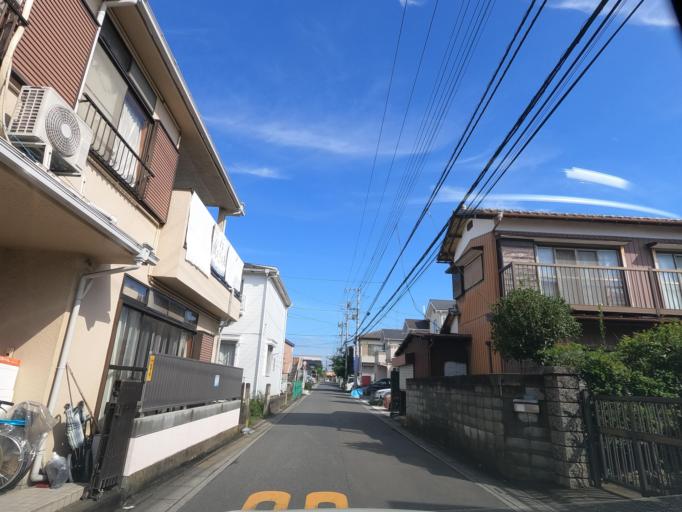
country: JP
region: Saitama
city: Yono
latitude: 35.8808
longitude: 139.6107
